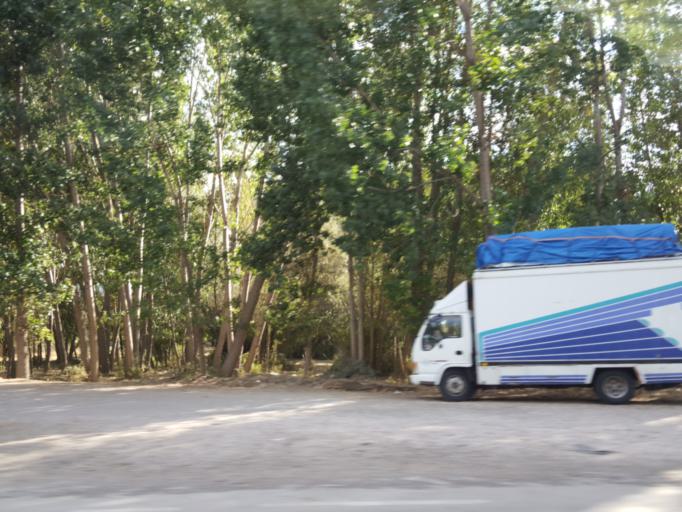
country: TR
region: Tokat
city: Yesilyurt
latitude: 40.0081
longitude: 36.2029
